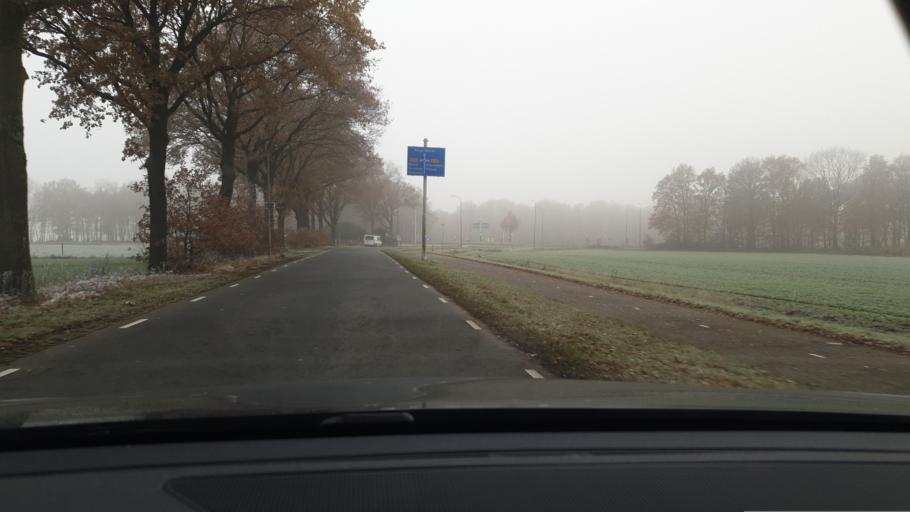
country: NL
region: North Brabant
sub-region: Gemeente Bladel en Netersel
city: Bladel
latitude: 51.3870
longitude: 5.1582
